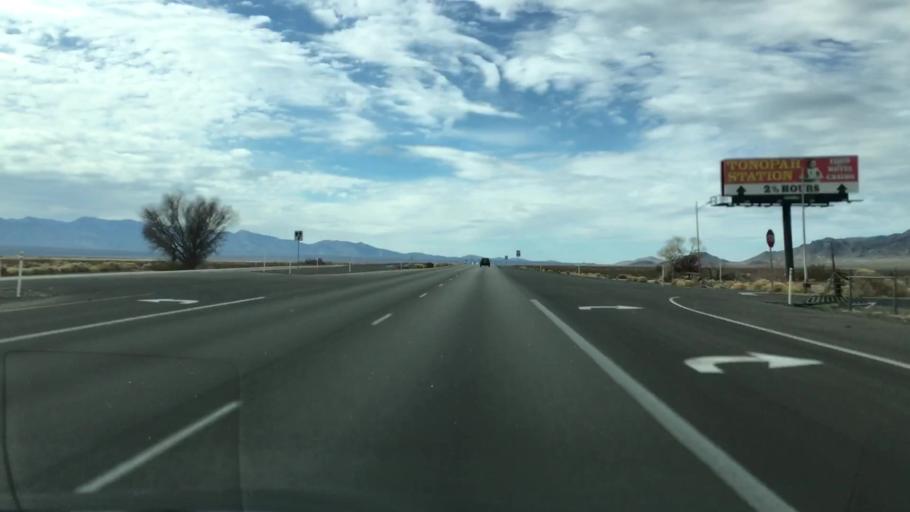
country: US
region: Nevada
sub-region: Nye County
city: Pahrump
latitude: 36.5778
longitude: -115.7275
